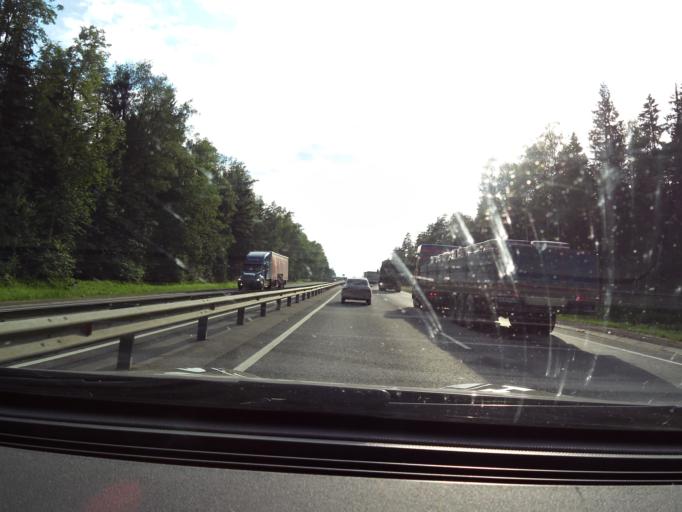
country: RU
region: Vladimir
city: Kameshkovo
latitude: 56.1976
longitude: 41.0192
